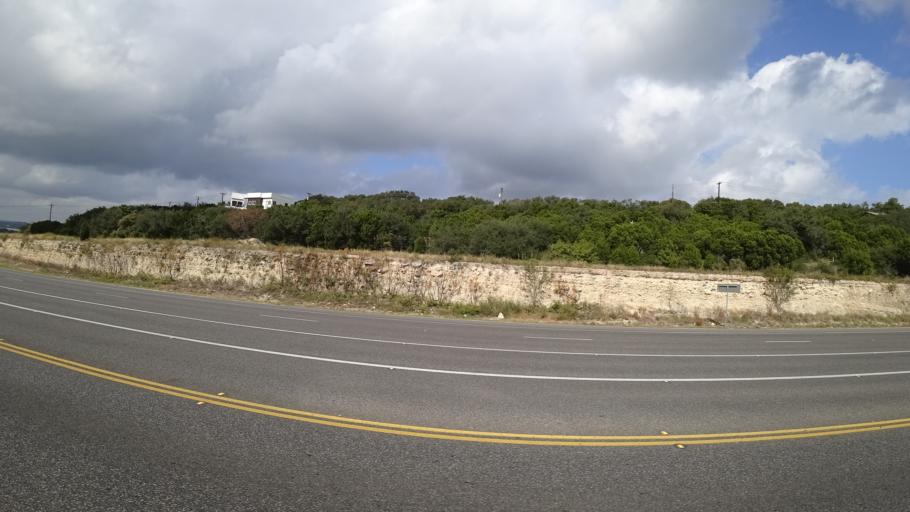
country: US
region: Texas
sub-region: Travis County
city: Hudson Bend
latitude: 30.3902
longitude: -97.8802
